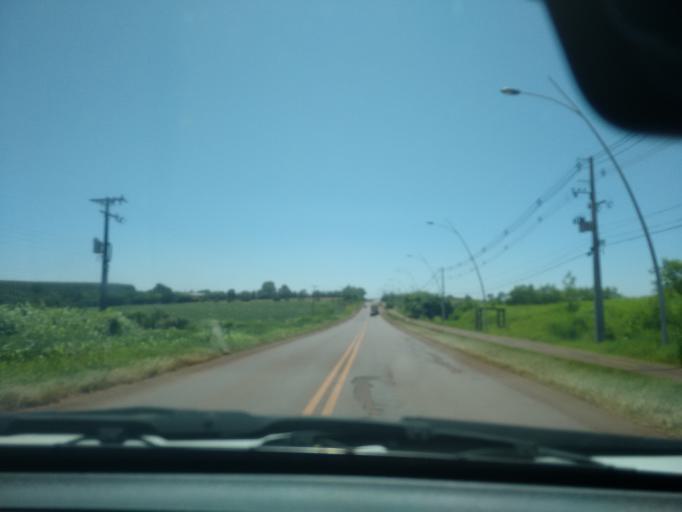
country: BR
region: Parana
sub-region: Marechal Candido Rondon
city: Marechal Candido Rondon
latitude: -24.5575
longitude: -54.1012
